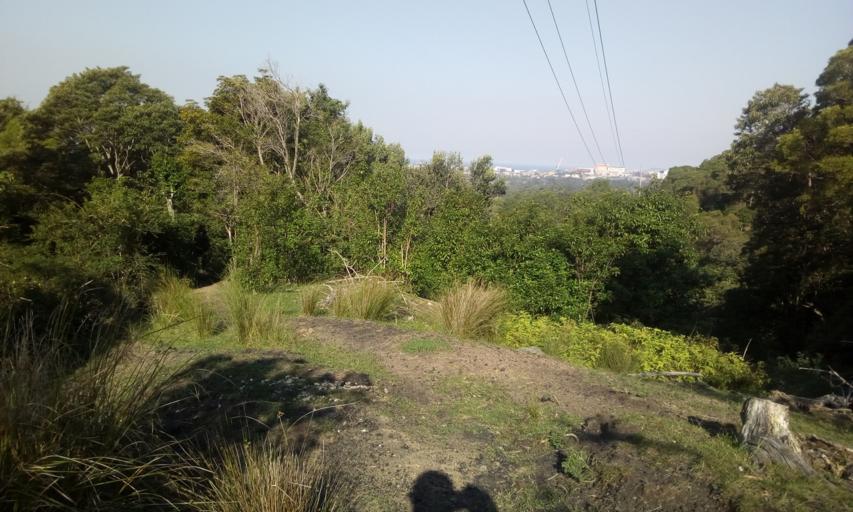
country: AU
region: New South Wales
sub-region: Wollongong
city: Mount Ousley
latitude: -34.4033
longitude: 150.8698
